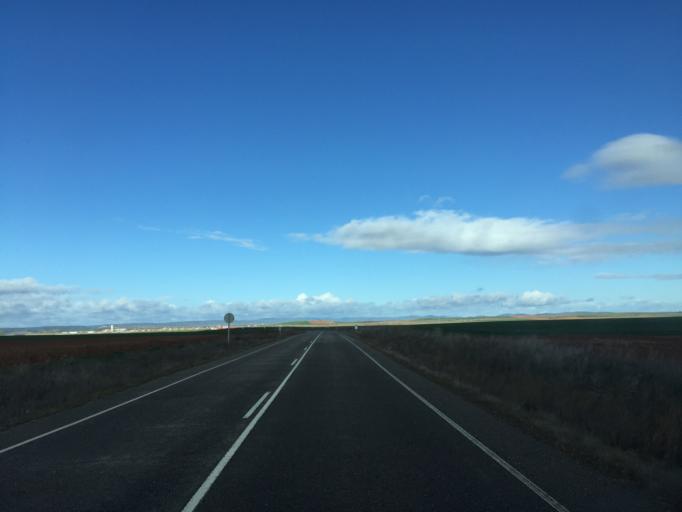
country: ES
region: Castille and Leon
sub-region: Provincia de Zamora
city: Manganeses de la Lampreana
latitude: 41.7596
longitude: -5.7326
